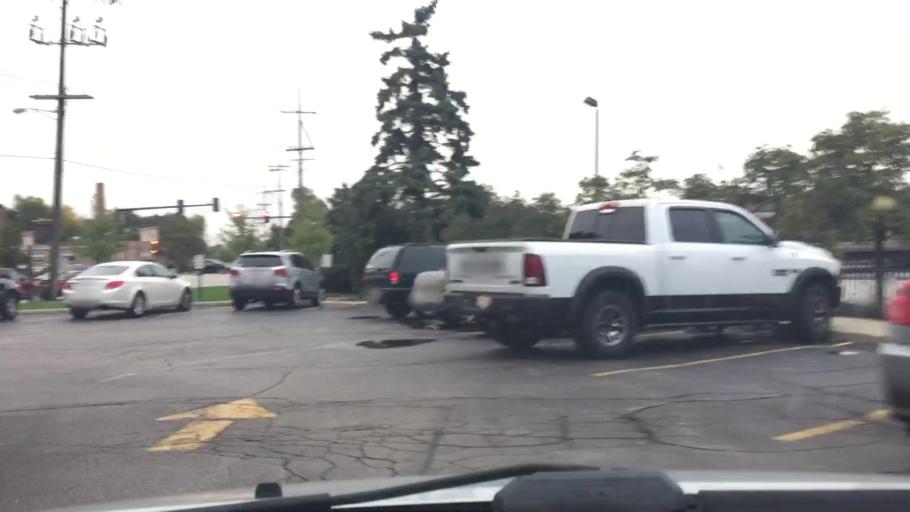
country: US
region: Illinois
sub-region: Kane County
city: Saint Charles
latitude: 41.9131
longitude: -88.3127
